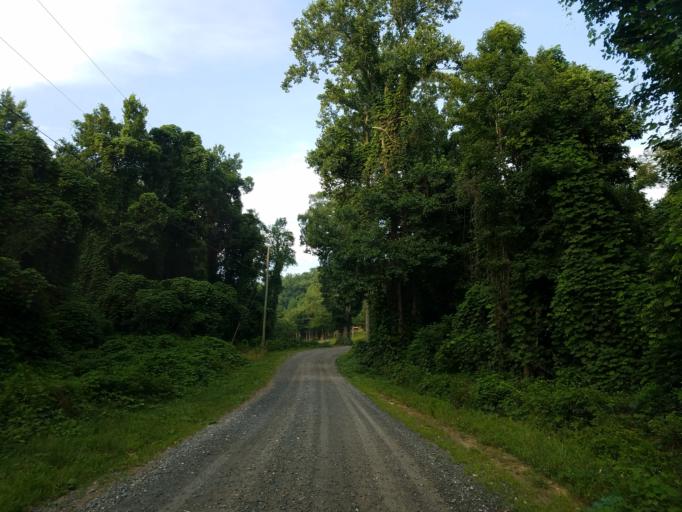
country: US
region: Georgia
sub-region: Pickens County
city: Jasper
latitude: 34.5417
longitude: -84.4539
